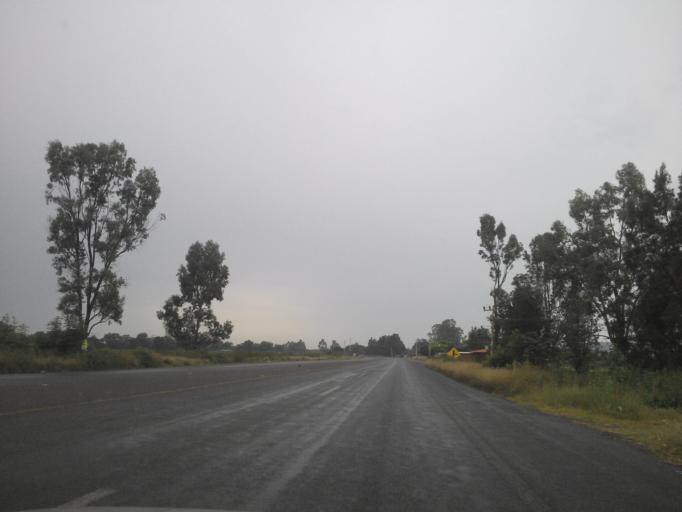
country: MX
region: Jalisco
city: Capilla de Guadalupe
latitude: 20.8529
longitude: -102.6154
